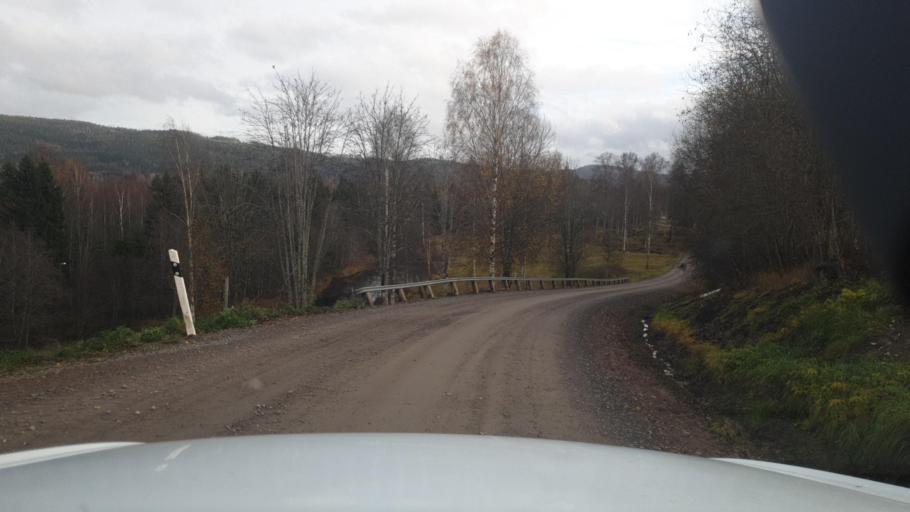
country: SE
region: Vaermland
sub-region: Torsby Kommun
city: Torsby
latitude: 59.9485
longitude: 12.8992
